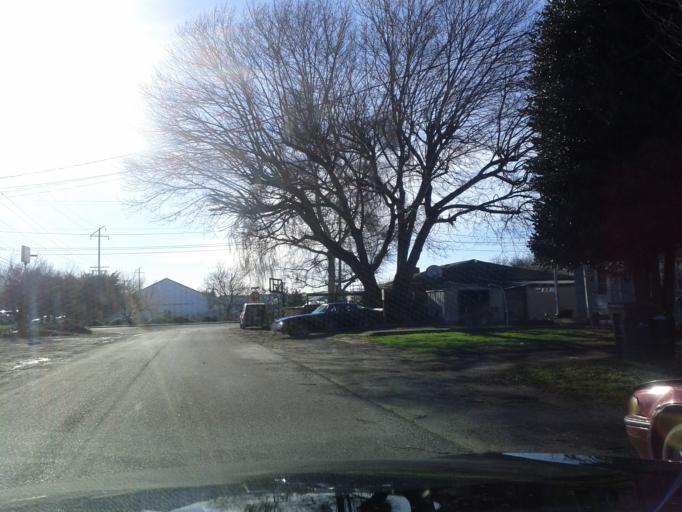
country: US
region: Washington
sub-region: Skagit County
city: Burlington
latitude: 48.4704
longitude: -122.3325
